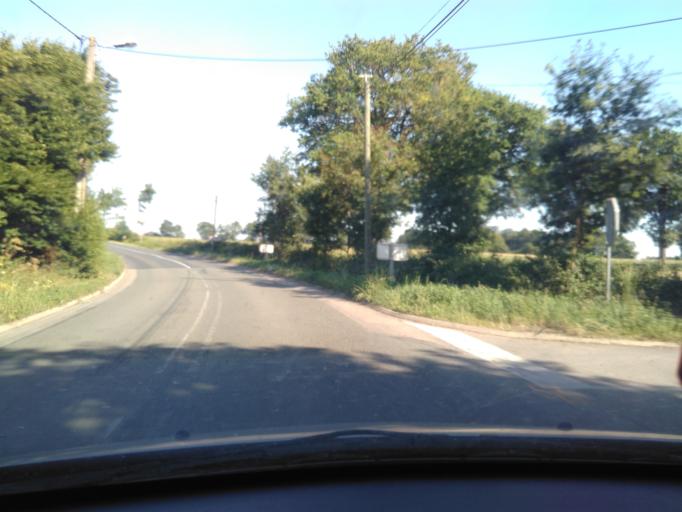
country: FR
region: Pays de la Loire
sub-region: Departement de la Vendee
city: Dompierre-sur-Yon
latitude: 46.7343
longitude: -1.3797
